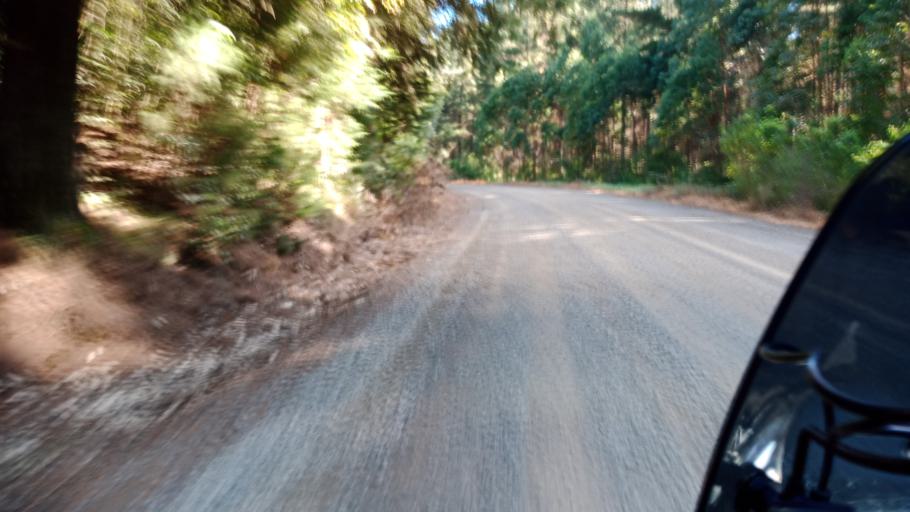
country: NZ
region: Hawke's Bay
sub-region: Wairoa District
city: Wairoa
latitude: -38.9247
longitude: 177.2133
